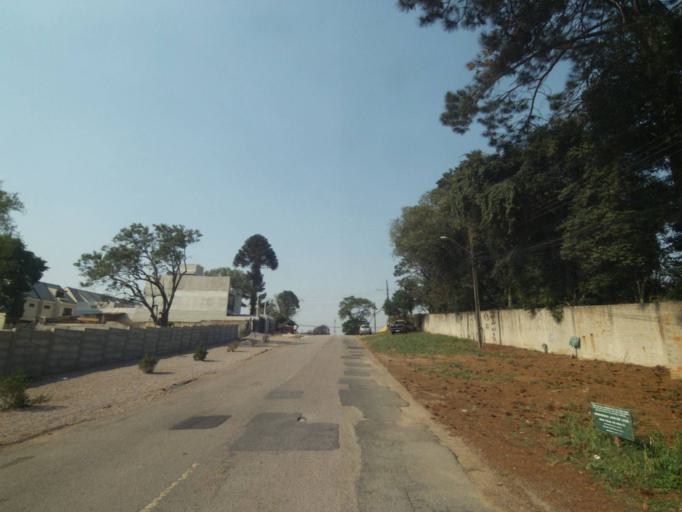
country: BR
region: Parana
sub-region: Sao Jose Dos Pinhais
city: Sao Jose dos Pinhais
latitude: -25.5215
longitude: -49.2535
